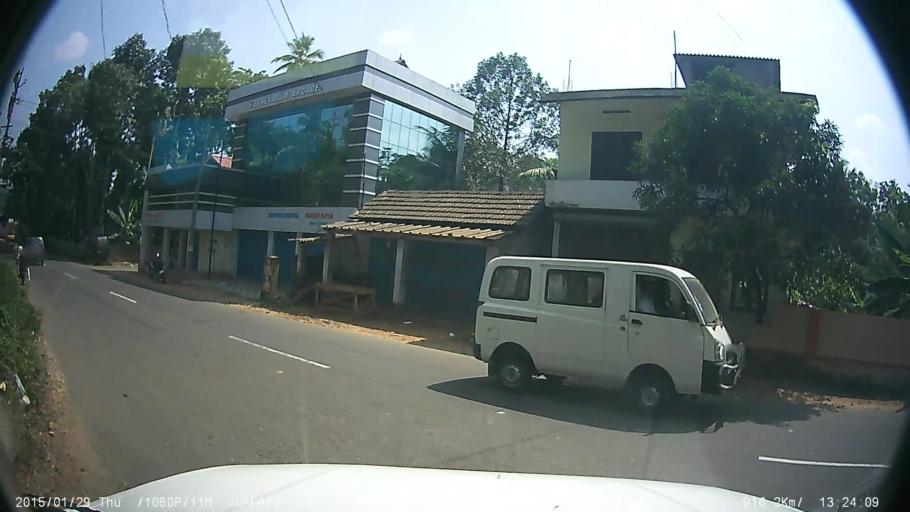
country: IN
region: Kerala
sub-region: Kottayam
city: Palackattumala
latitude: 9.7568
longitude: 76.5568
